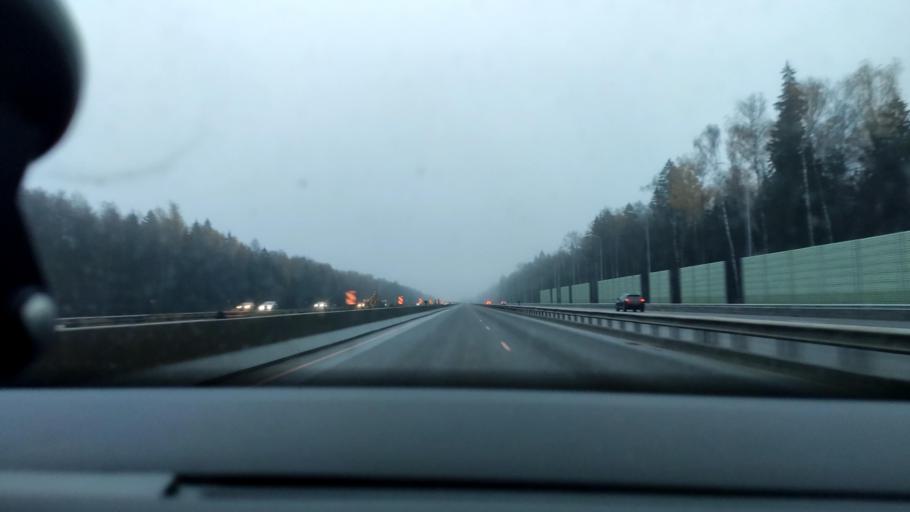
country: RU
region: Moskovskaya
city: Bol'shiye Vyazemy
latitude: 55.5918
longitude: 36.9087
